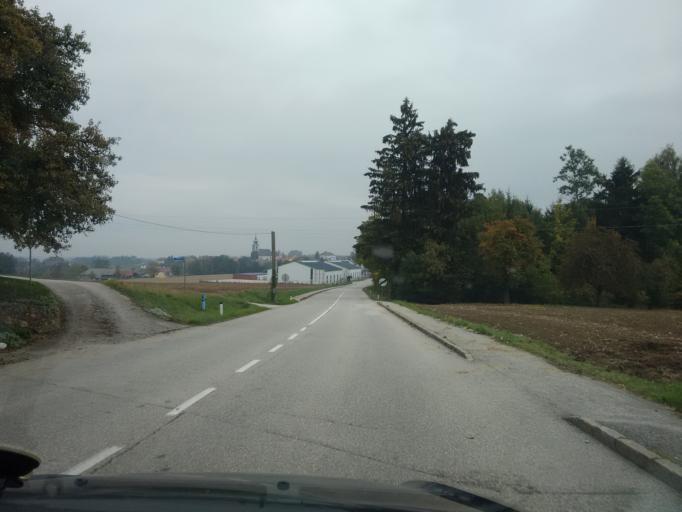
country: AT
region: Upper Austria
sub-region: Wels-Land
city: Sattledt
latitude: 48.0192
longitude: 14.0686
